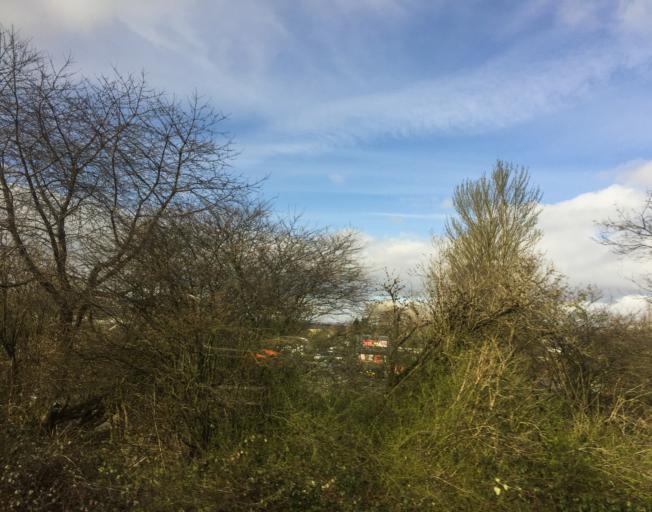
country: GB
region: Scotland
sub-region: Glasgow City
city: Glasgow
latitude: 55.8986
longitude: -4.2891
